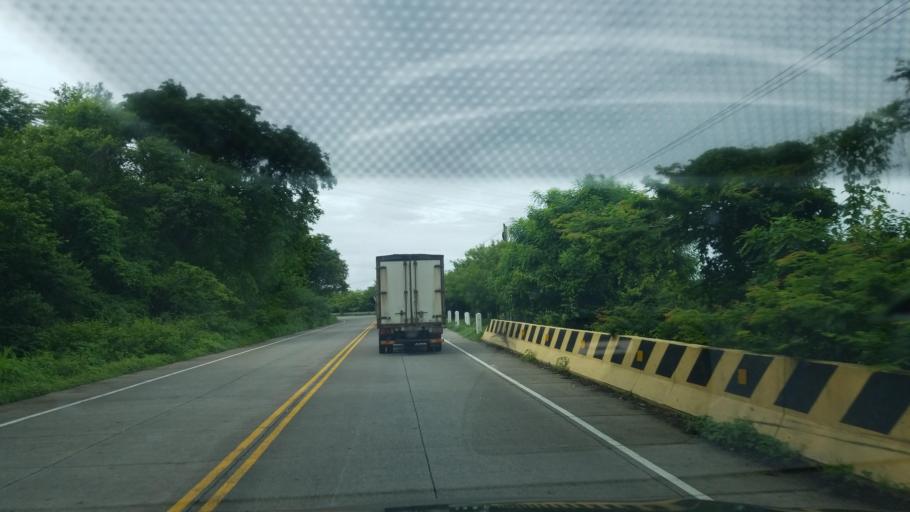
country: HN
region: Francisco Morazan
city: El Porvenir
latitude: 13.6812
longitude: -87.3555
